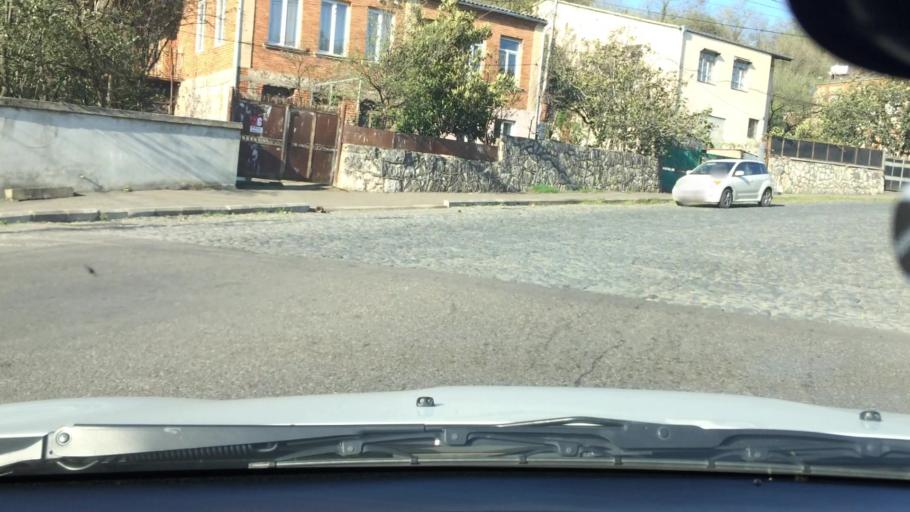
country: GE
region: Imereti
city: Kutaisi
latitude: 42.2631
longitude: 42.7225
